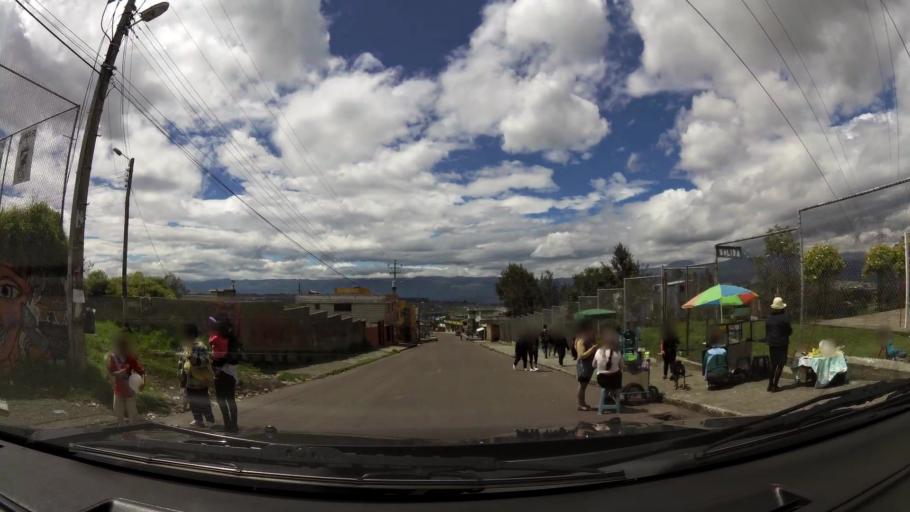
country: EC
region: Pichincha
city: Sangolqui
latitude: -0.3433
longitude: -78.5637
